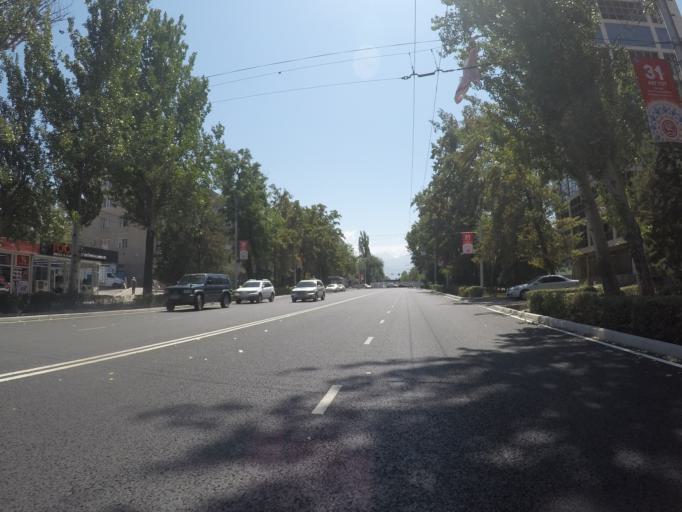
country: KG
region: Chuy
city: Bishkek
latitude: 42.8692
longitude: 74.5875
